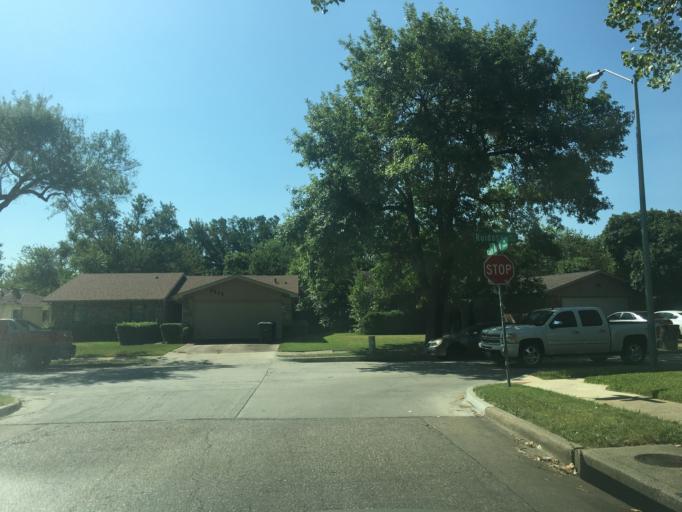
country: US
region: Texas
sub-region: Dallas County
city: Garland
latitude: 32.8534
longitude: -96.6586
